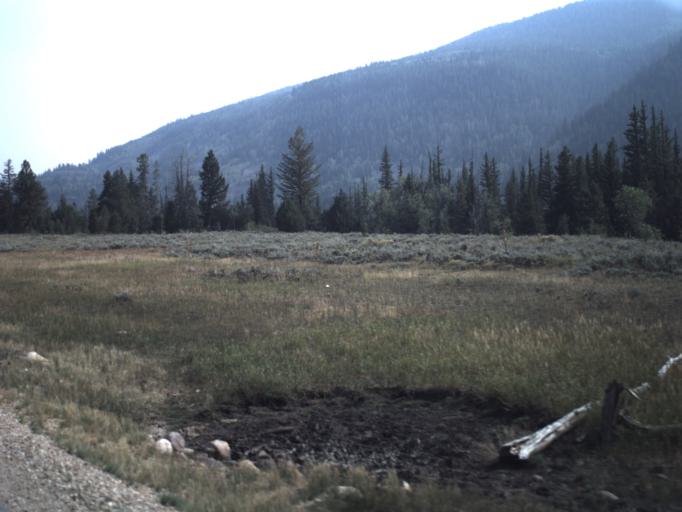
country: US
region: Utah
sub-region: Summit County
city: Francis
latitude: 40.5939
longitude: -111.0731
